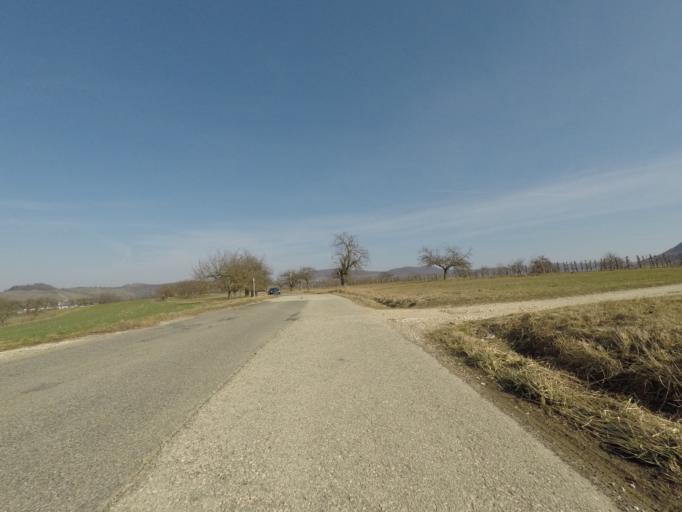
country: DE
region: Baden-Wuerttemberg
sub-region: Tuebingen Region
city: Metzingen
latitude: 48.5188
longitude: 9.2980
